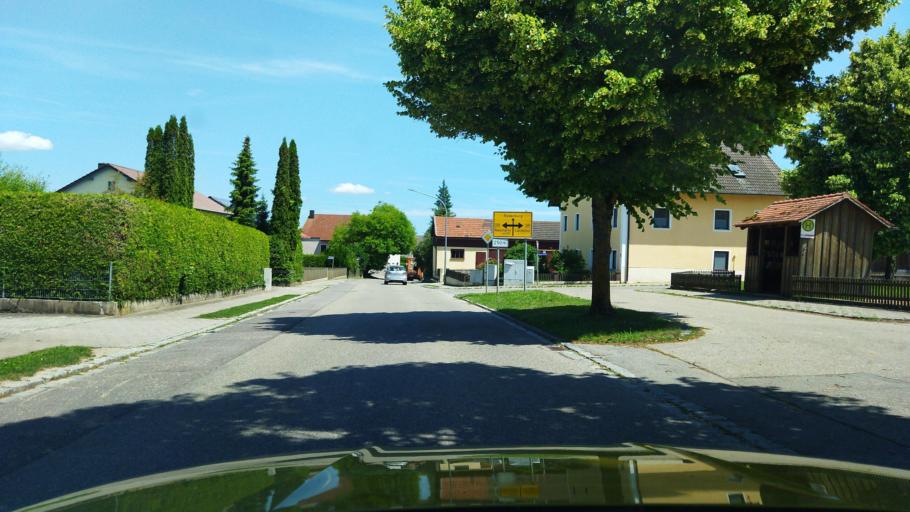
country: DE
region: Bavaria
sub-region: Upper Palatinate
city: Dietfurt
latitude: 48.9437
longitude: 11.5627
